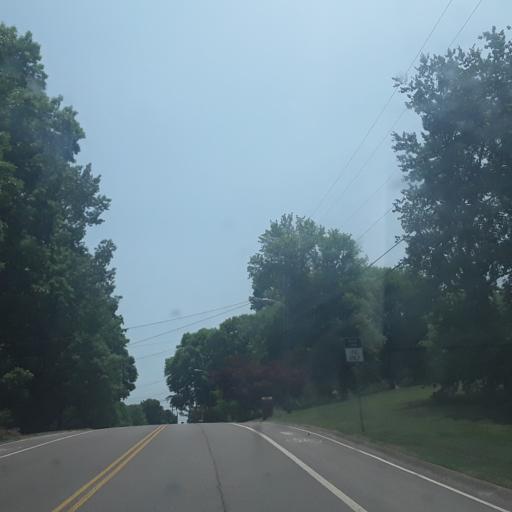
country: US
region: Tennessee
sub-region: Williamson County
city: Brentwood
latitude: 36.0574
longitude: -86.7601
